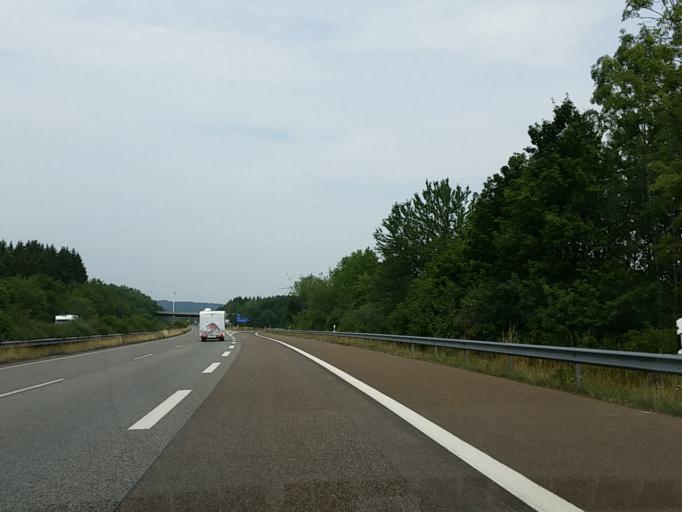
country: DE
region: Rheinland-Pfalz
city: Hermeskeil
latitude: 49.6723
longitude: 6.9205
